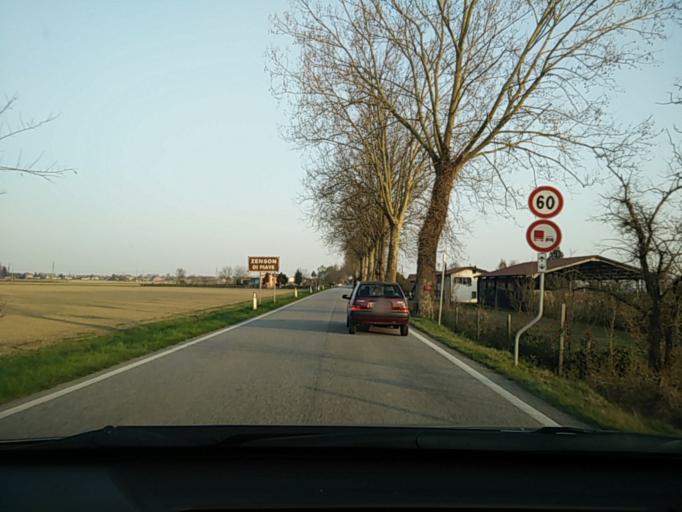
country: IT
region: Veneto
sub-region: Provincia di Treviso
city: Zenson di Piave
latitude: 45.6872
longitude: 12.4659
